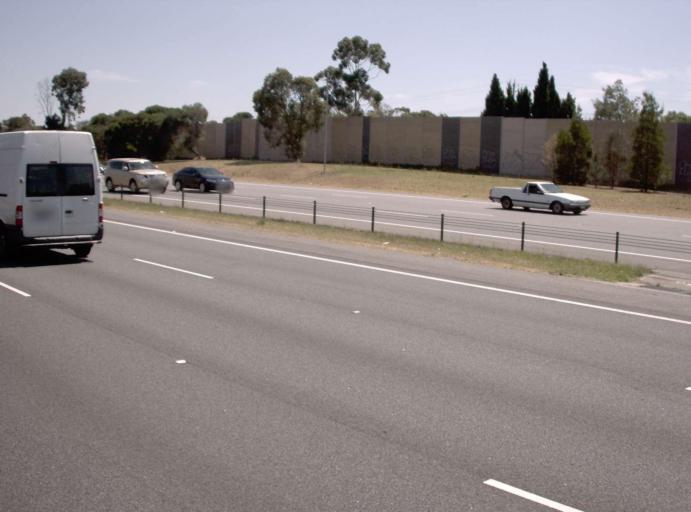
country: AU
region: Victoria
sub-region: Monash
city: Notting Hill
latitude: -37.9133
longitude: 145.1661
